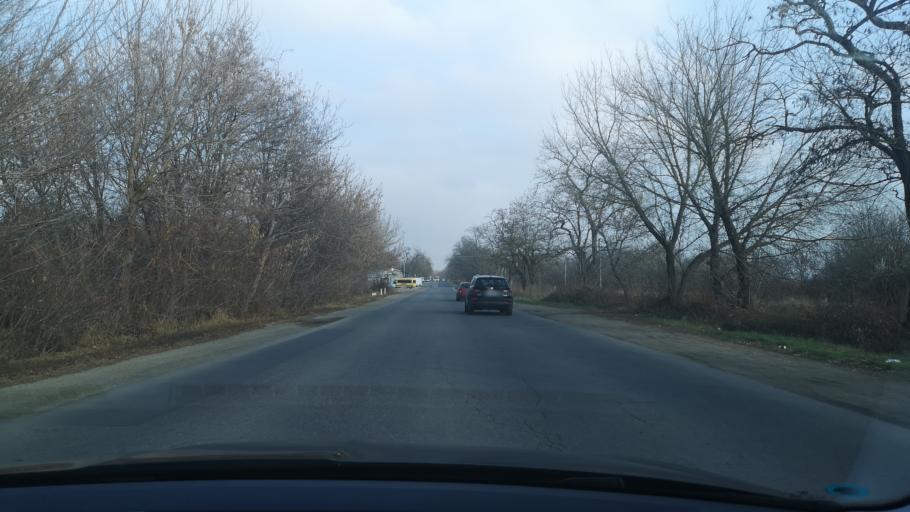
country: MD
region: Balti
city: Balti
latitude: 47.7814
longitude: 27.9623
